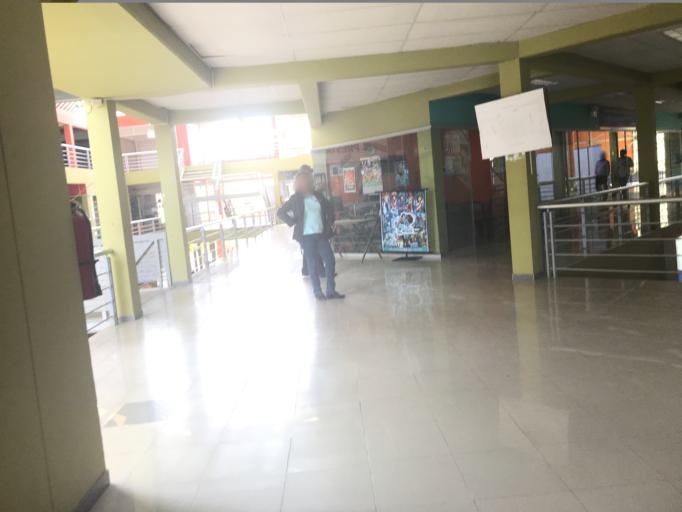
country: PE
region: Lambayeque
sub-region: Provincia de Chiclayo
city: Santa Rosa
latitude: -6.7753
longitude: -79.8317
